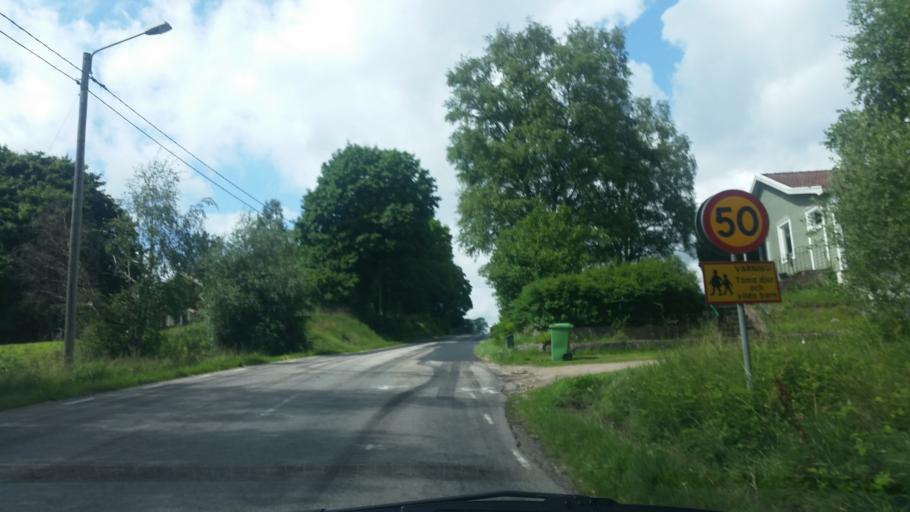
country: SE
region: Joenkoeping
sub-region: Gislaveds Kommun
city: Reftele
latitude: 57.1792
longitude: 13.5732
